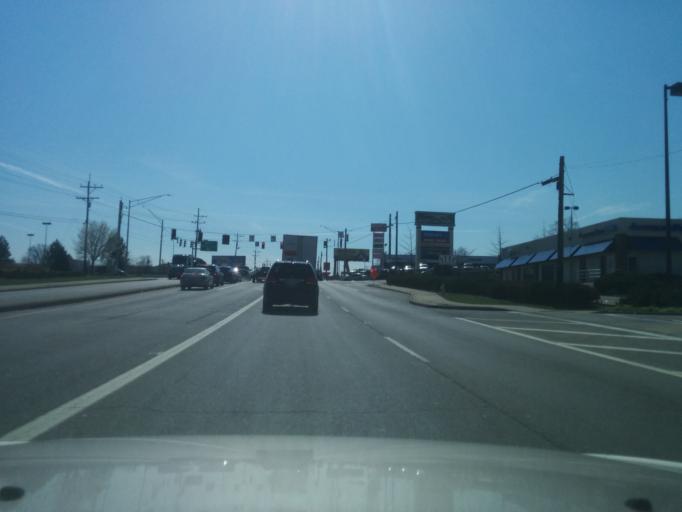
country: US
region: Ohio
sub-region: Hamilton County
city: Groesbeck
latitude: 39.2246
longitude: -84.5878
